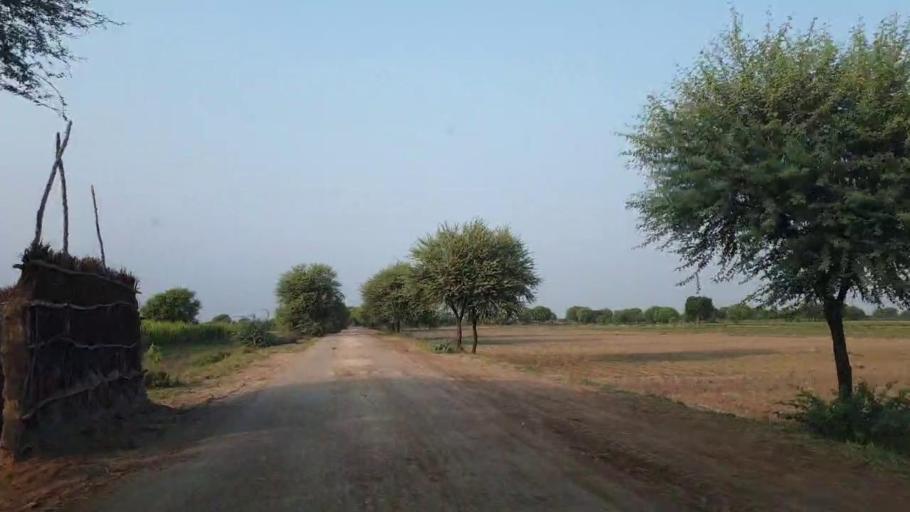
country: PK
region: Sindh
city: Rajo Khanani
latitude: 25.0410
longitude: 68.9644
